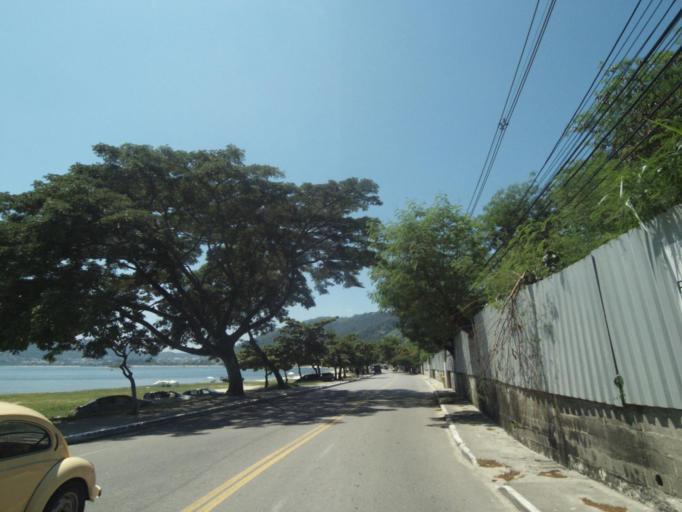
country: BR
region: Rio de Janeiro
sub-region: Niteroi
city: Niteroi
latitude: -22.9363
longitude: -43.1059
